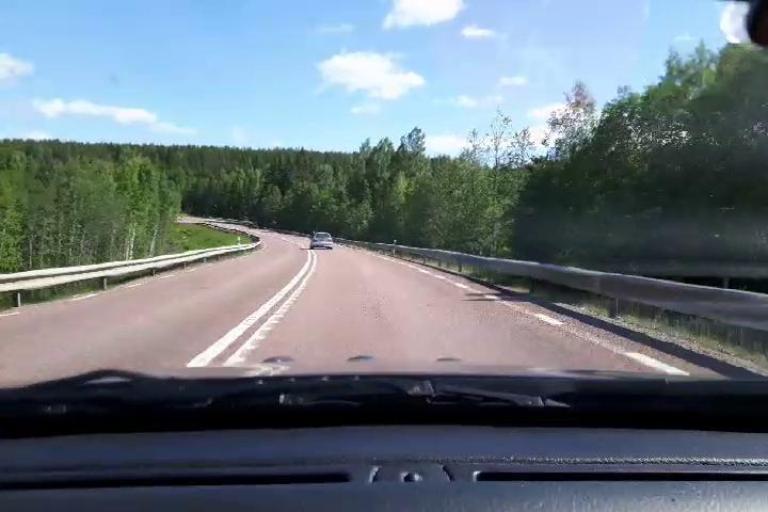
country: SE
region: Gaevleborg
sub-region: Hudiksvalls Kommun
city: Sorforsa
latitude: 61.7589
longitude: 16.7855
